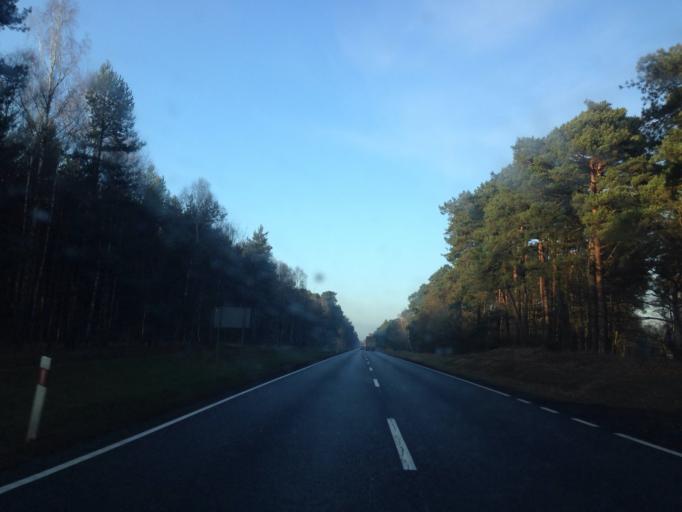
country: PL
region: Kujawsko-Pomorskie
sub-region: Powiat torunski
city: Wielka Nieszawka
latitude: 53.0096
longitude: 18.4400
